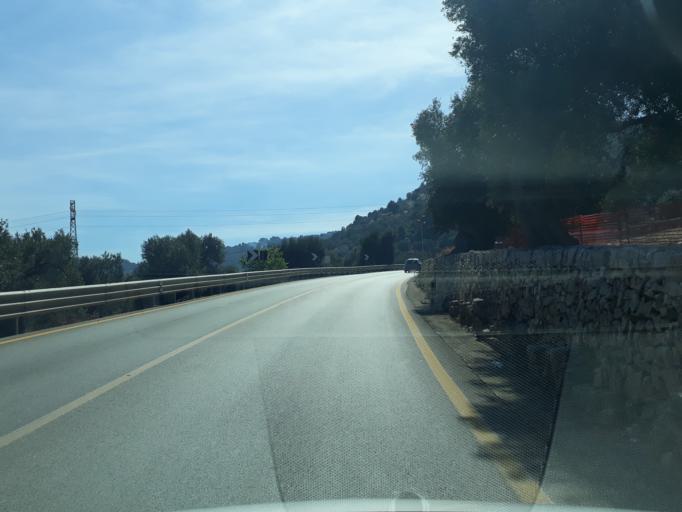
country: IT
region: Apulia
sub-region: Provincia di Brindisi
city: Lamie di Olimpie-Selva
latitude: 40.8187
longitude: 17.3457
